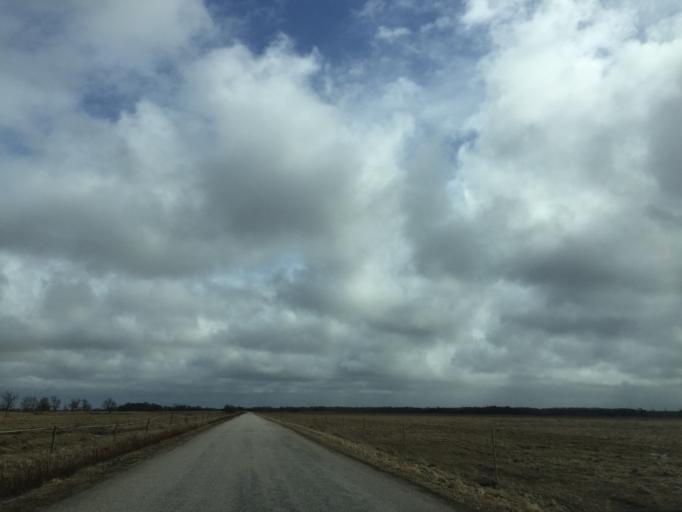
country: EE
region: Laeaene
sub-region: Lihula vald
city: Lihula
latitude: 58.7310
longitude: 23.8765
